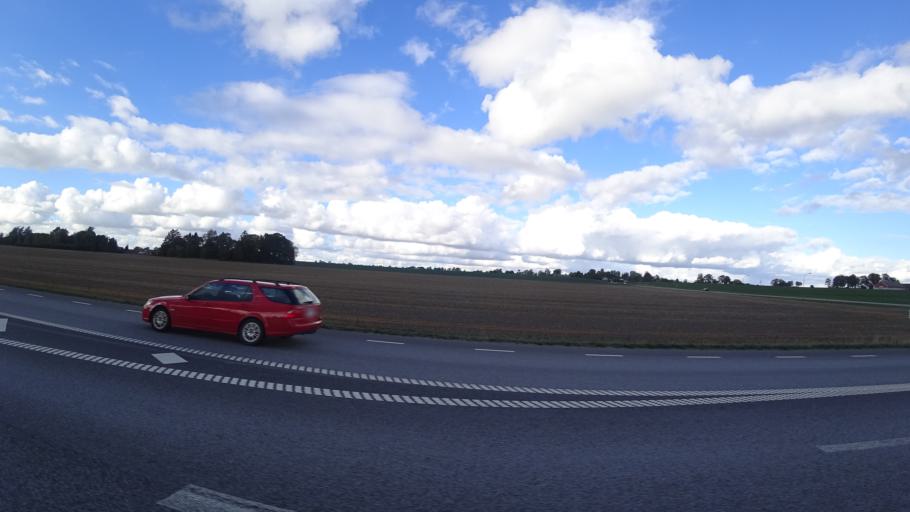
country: SE
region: Skane
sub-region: Kavlinge Kommun
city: Kaevlinge
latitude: 55.7973
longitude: 13.1477
